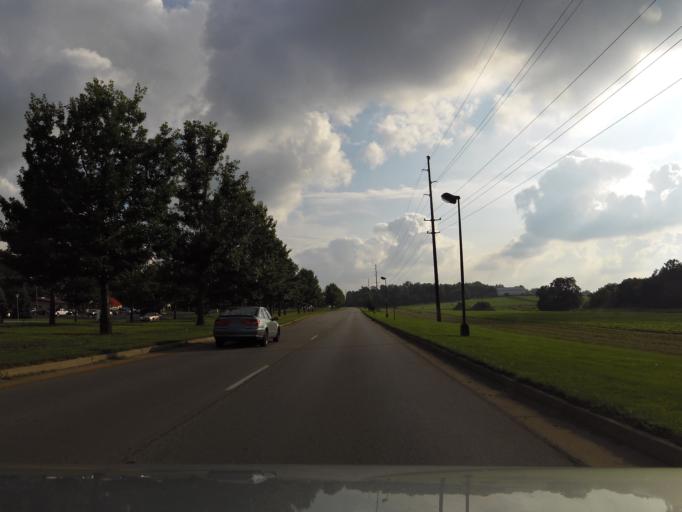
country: US
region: Kentucky
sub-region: Bourbon County
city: Paris
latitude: 38.1899
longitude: -84.2833
